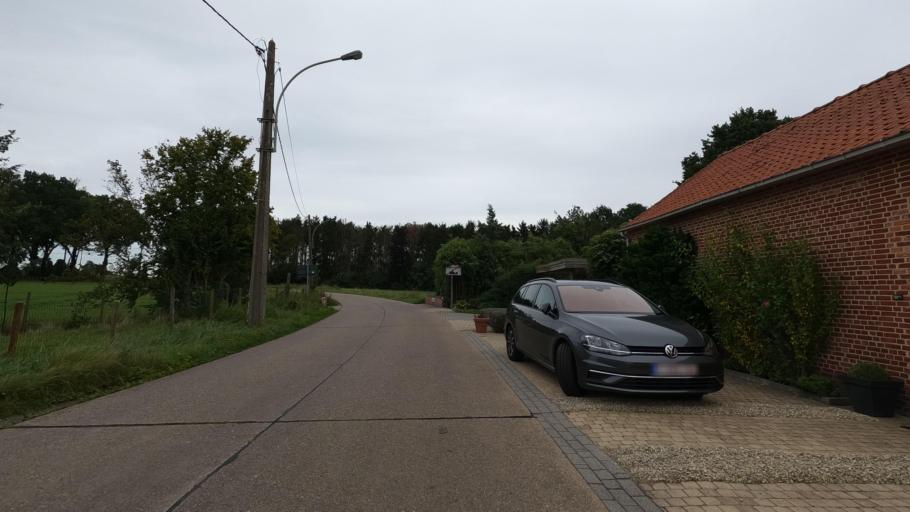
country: BE
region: Flanders
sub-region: Provincie Antwerpen
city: Rijkevorsel
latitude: 51.3506
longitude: 4.7713
